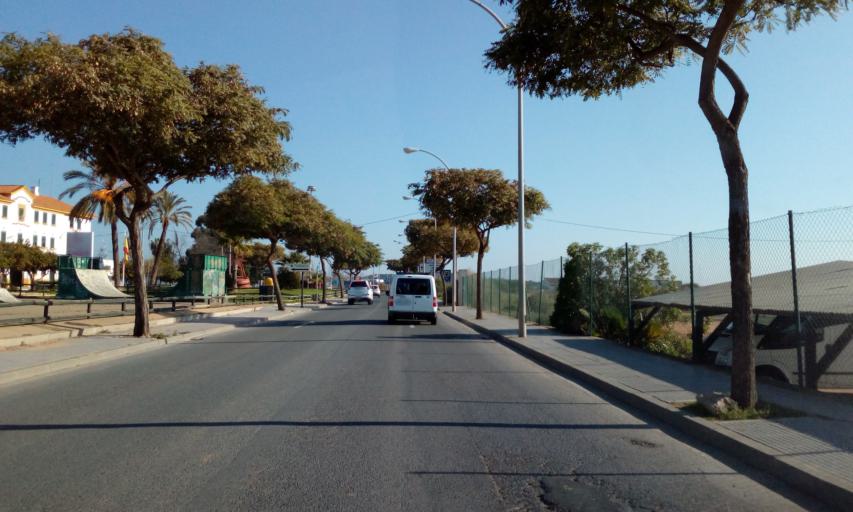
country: ES
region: Andalusia
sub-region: Provincia de Huelva
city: Ayamonte
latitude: 37.2155
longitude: -7.3955
